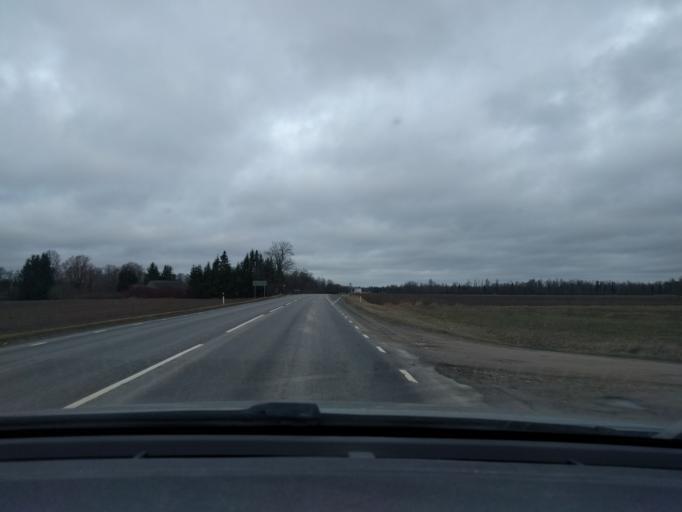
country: EE
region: Viljandimaa
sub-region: Viljandi linn
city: Viljandi
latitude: 58.4586
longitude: 25.5934
